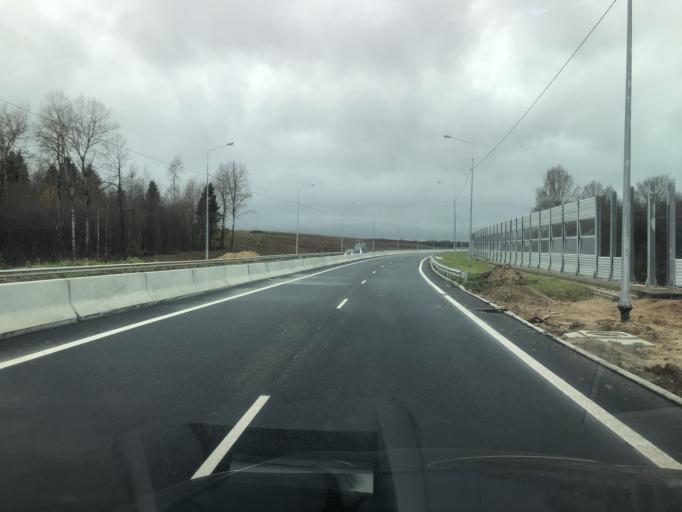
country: RU
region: Moskovskaya
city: Sergiyev Posad
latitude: 56.3363
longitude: 38.1119
